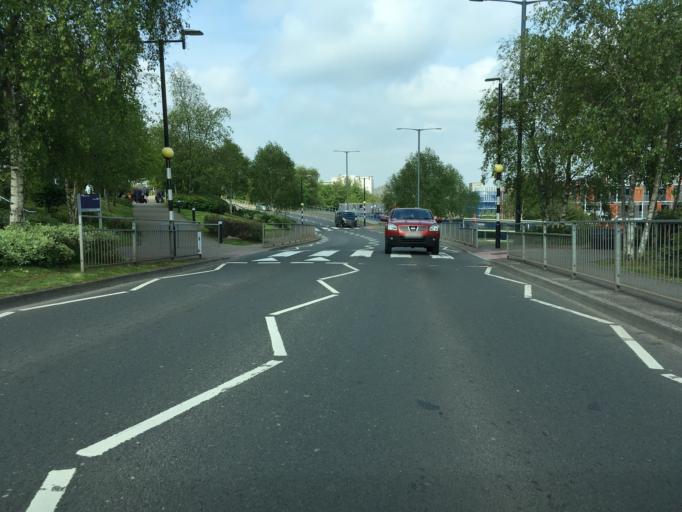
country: GB
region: England
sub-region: North Somerset
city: Butcombe
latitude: 51.3870
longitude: -2.7100
